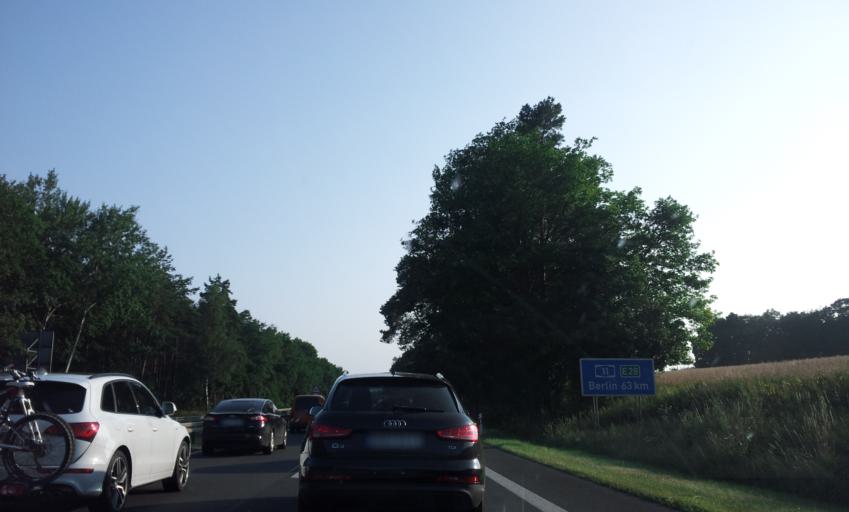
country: DE
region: Brandenburg
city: Melchow
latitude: 52.8778
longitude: 13.6959
